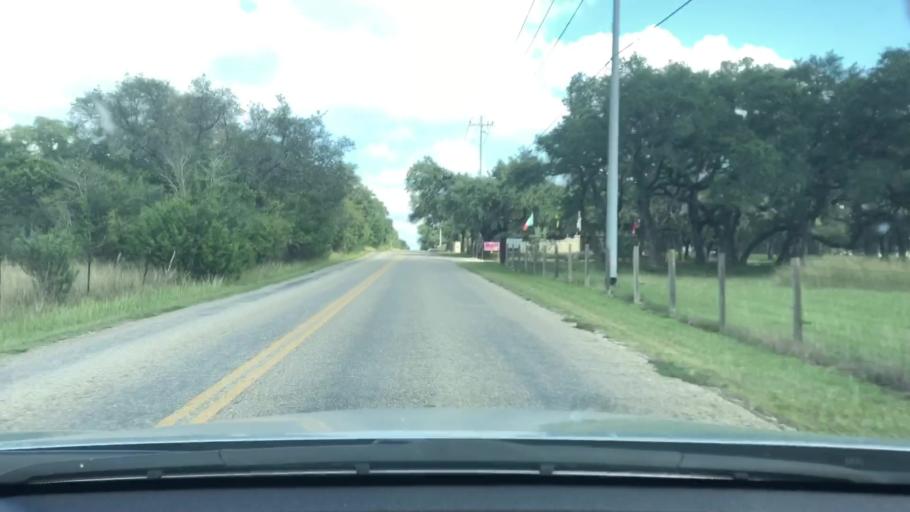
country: US
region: Texas
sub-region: Bexar County
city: Fair Oaks Ranch
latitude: 29.7854
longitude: -98.6422
